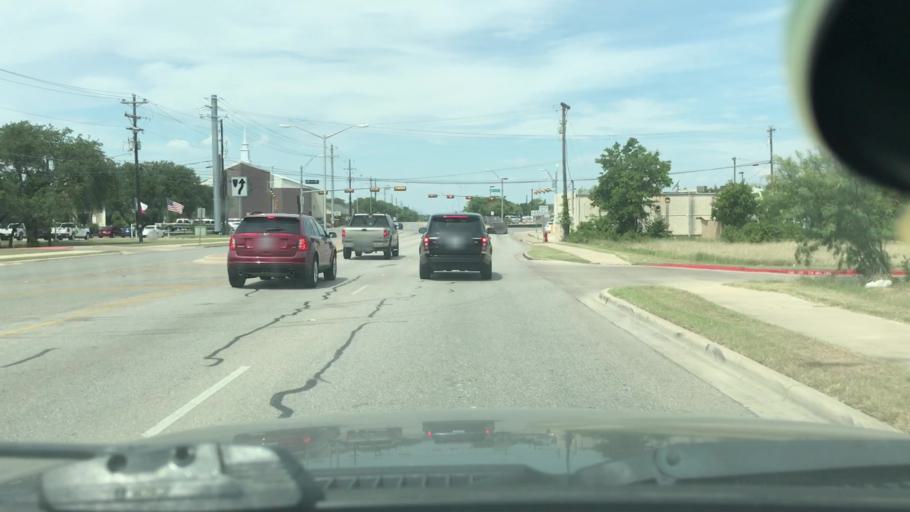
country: US
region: Texas
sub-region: Williamson County
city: Cedar Park
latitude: 30.5334
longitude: -97.8339
